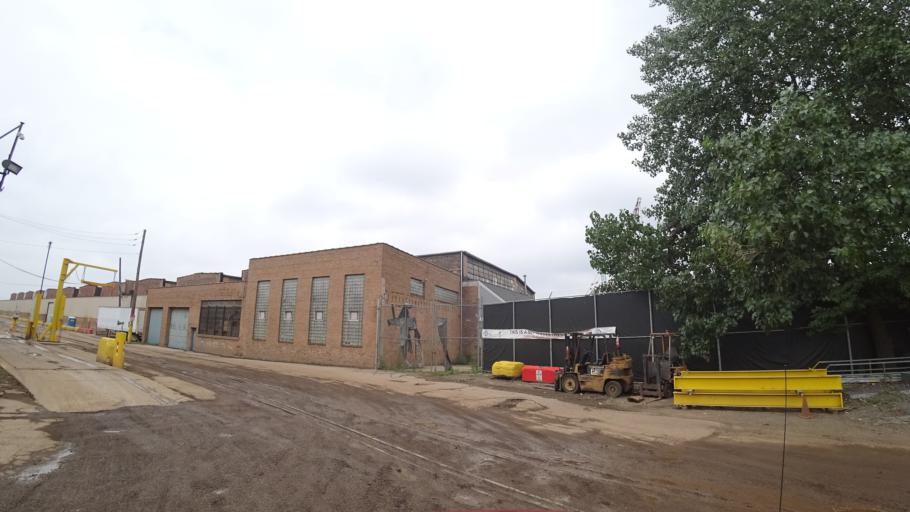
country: US
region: Illinois
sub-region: Cook County
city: Chicago
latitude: 41.8452
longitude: -87.6685
